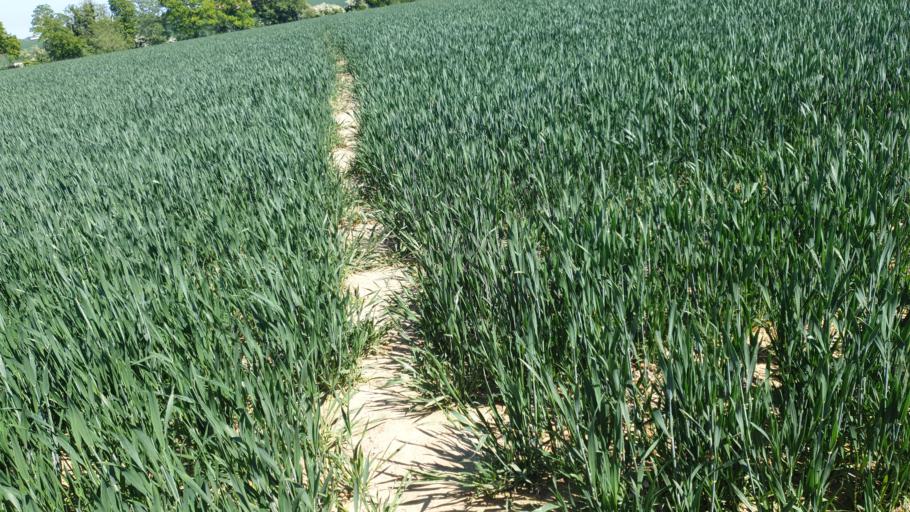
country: GB
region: England
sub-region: Essex
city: Great Bentley
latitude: 51.8597
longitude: 1.0482
